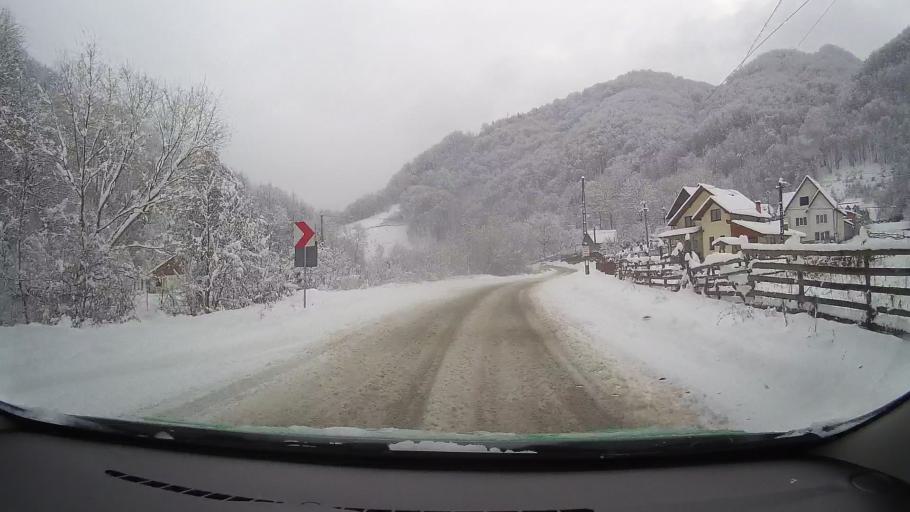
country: RO
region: Alba
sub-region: Comuna Sugag
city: Dobra
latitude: 45.7649
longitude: 23.6504
